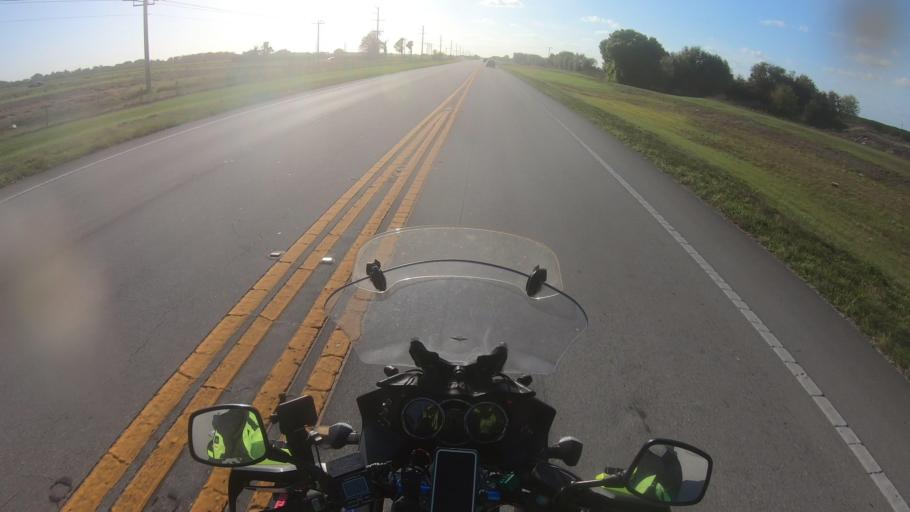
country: US
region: Florida
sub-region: DeSoto County
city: Southeast Arcadia
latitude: 27.2097
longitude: -81.6913
